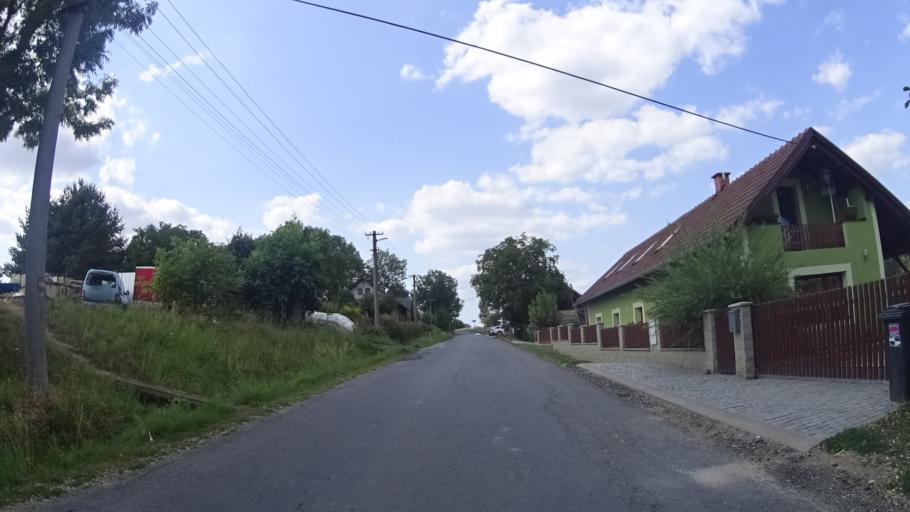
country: CZ
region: Kralovehradecky
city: Kopidlno
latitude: 50.3982
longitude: 15.2833
